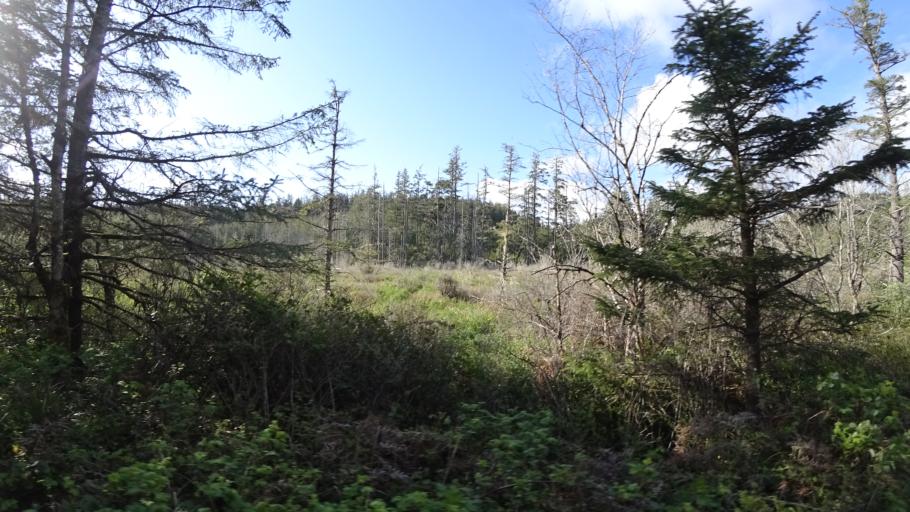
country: US
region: Oregon
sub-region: Douglas County
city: Reedsport
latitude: 43.7490
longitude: -124.1594
